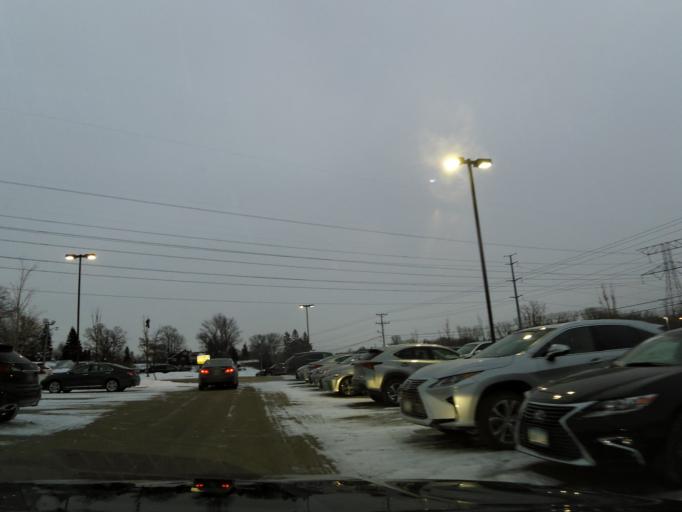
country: US
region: Minnesota
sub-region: Ramsey County
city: Vadnais Heights
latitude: 45.0333
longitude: -93.0459
